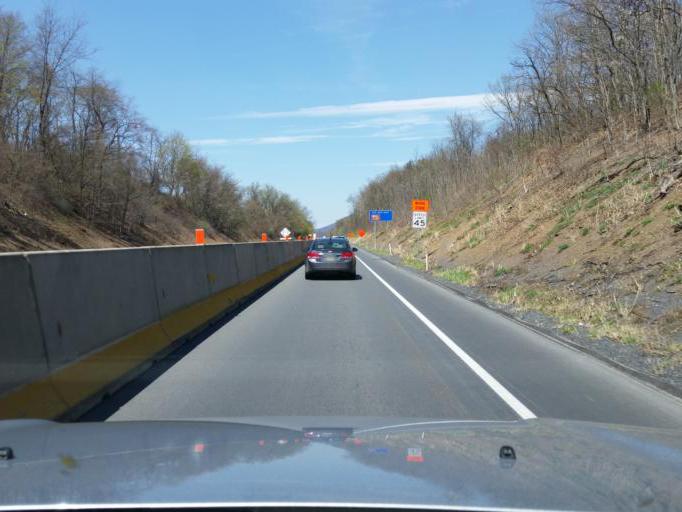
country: US
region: Pennsylvania
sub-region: Mifflin County
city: Lewistown
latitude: 40.5879
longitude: -77.5562
